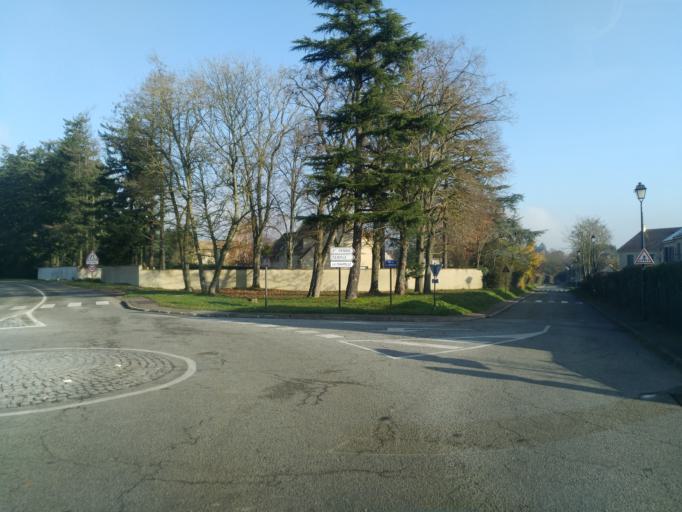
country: FR
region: Ile-de-France
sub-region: Departement des Yvelines
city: Feucherolles
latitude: 48.8774
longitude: 1.9794
